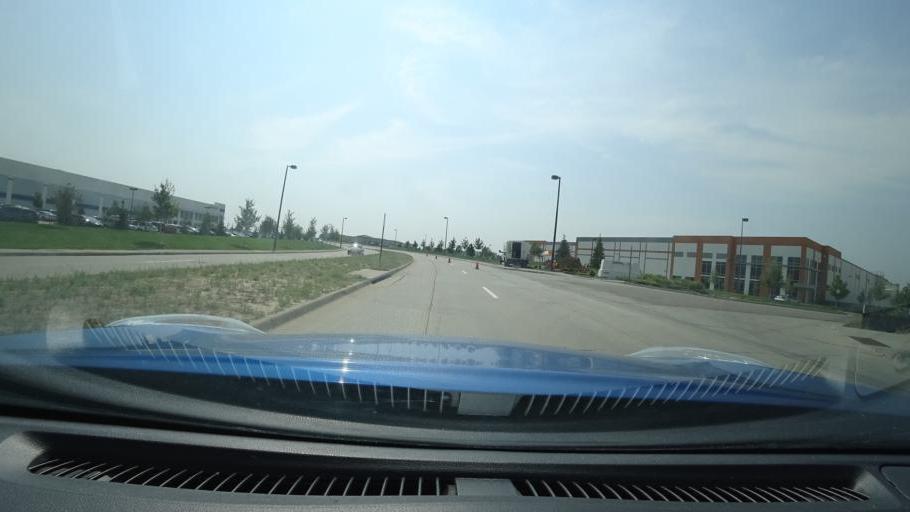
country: US
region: Colorado
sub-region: Adams County
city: Aurora
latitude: 39.7702
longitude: -104.7764
